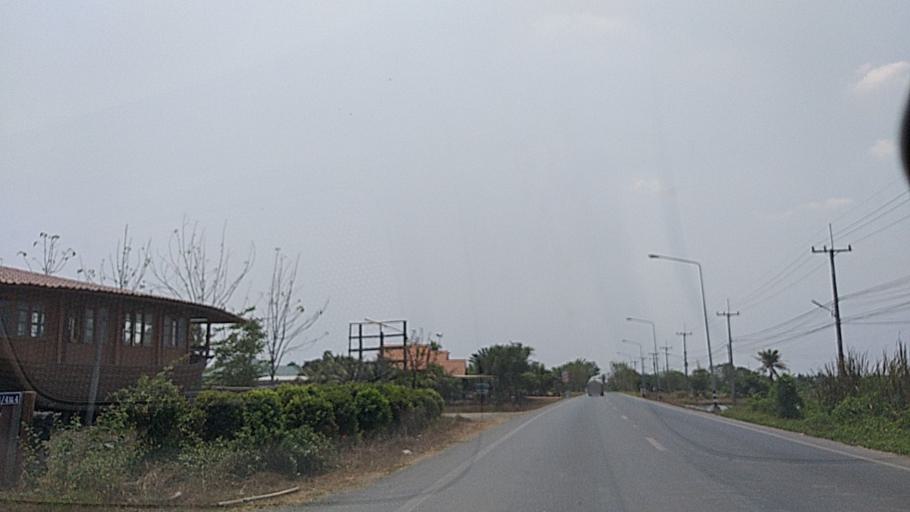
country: TH
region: Chachoengsao
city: Bang Nam Priao
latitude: 13.9373
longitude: 100.9781
